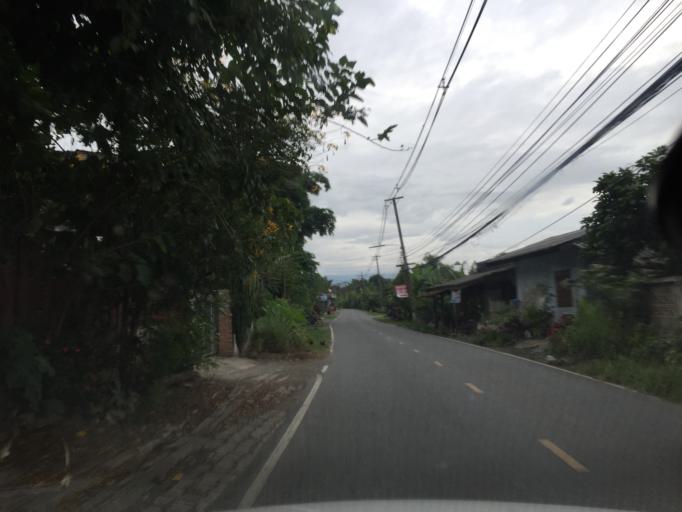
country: TH
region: Chiang Mai
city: Mae On
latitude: 18.8317
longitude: 99.1668
